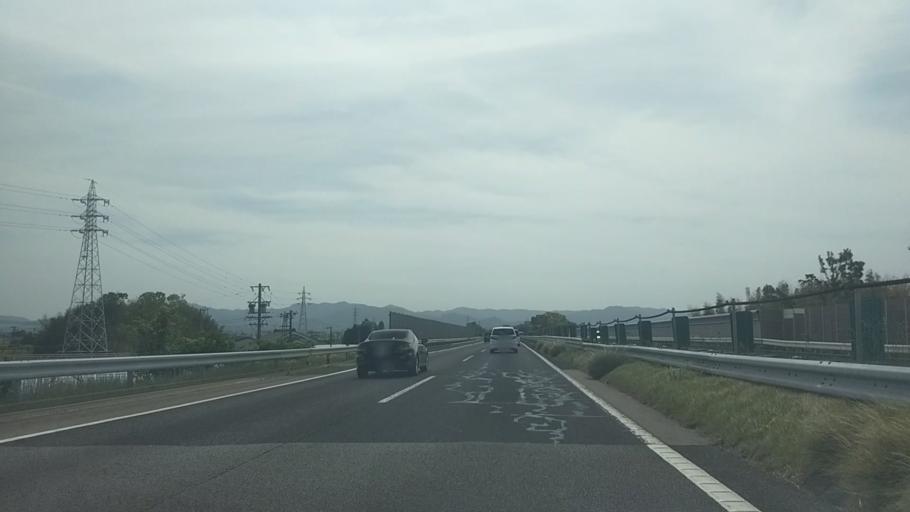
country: JP
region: Aichi
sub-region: Tokai-shi
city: Toyokawa
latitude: 34.8453
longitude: 137.3927
